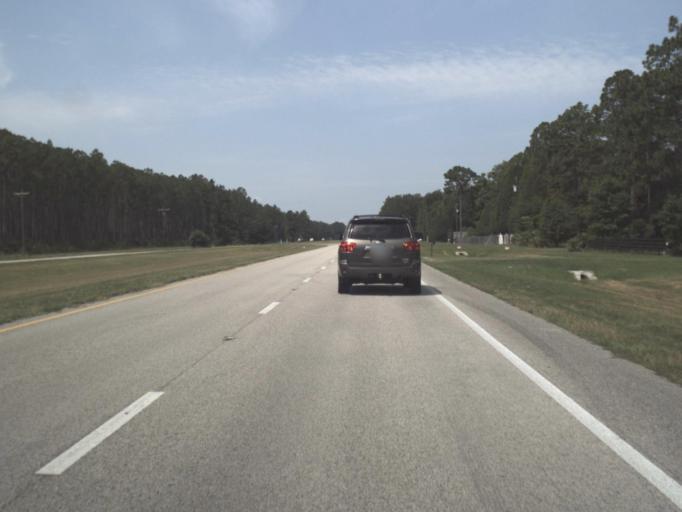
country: US
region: Florida
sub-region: Alachua County
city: Waldo
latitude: 29.7505
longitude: -82.2217
